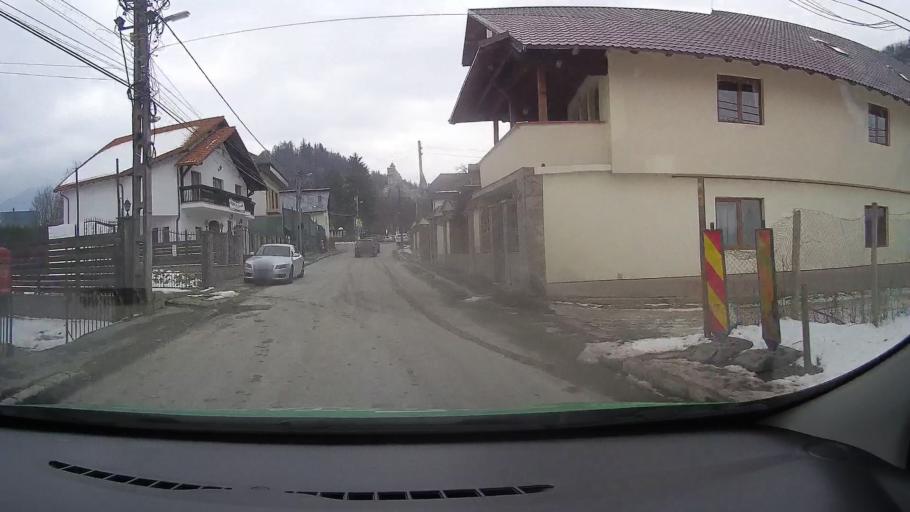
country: RO
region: Brasov
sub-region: Comuna Bran
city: Bran
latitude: 45.5184
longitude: 25.3665
